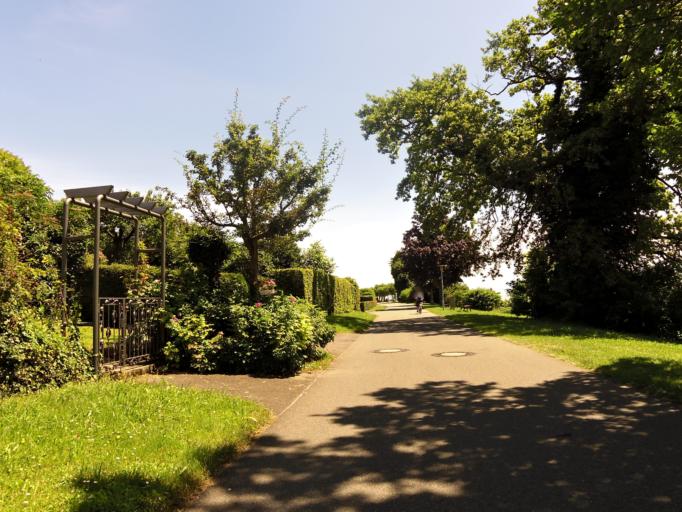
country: DE
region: Baden-Wuerttemberg
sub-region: Tuebingen Region
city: Hagnau
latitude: 47.6753
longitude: 9.3089
